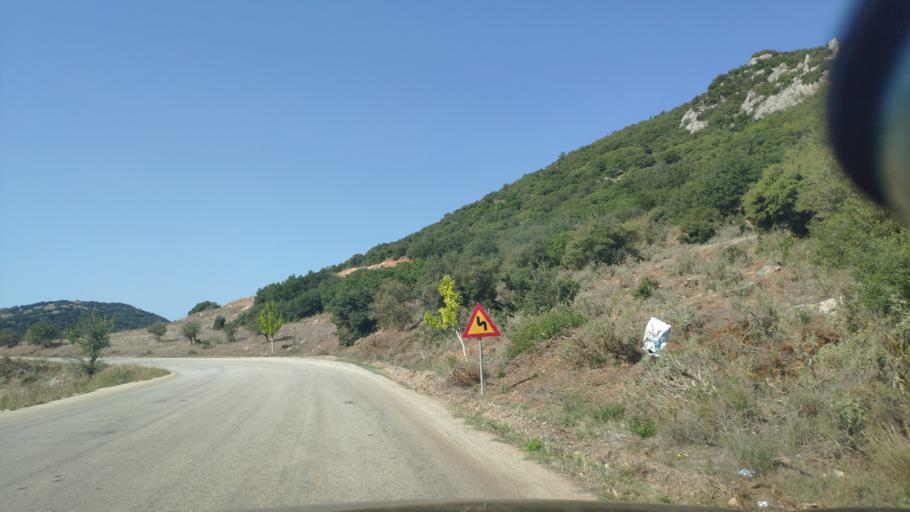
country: GR
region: Peloponnese
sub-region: Nomos Korinthias
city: Nemea
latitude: 37.8902
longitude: 22.5112
